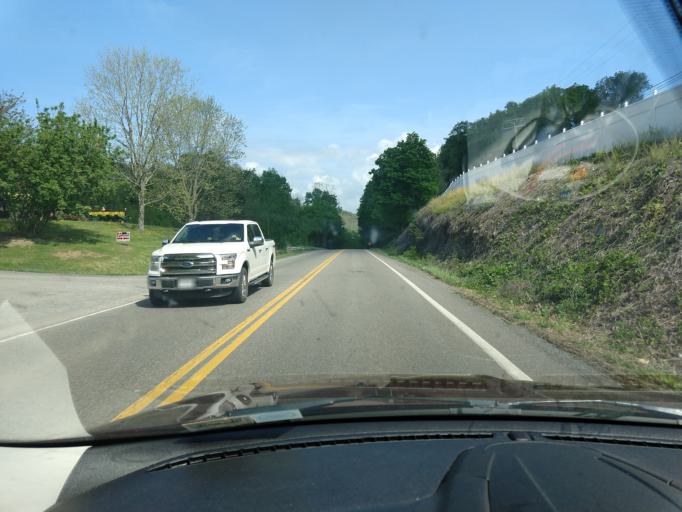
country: US
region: Virginia
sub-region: Russell County
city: Honaker
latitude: 36.9675
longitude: -81.9388
